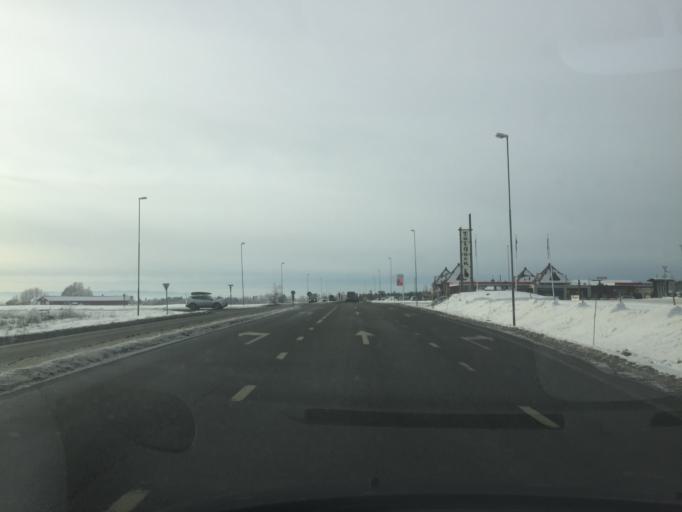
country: NO
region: Hedmark
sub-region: Loten
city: Loten
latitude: 60.8499
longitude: 11.3712
